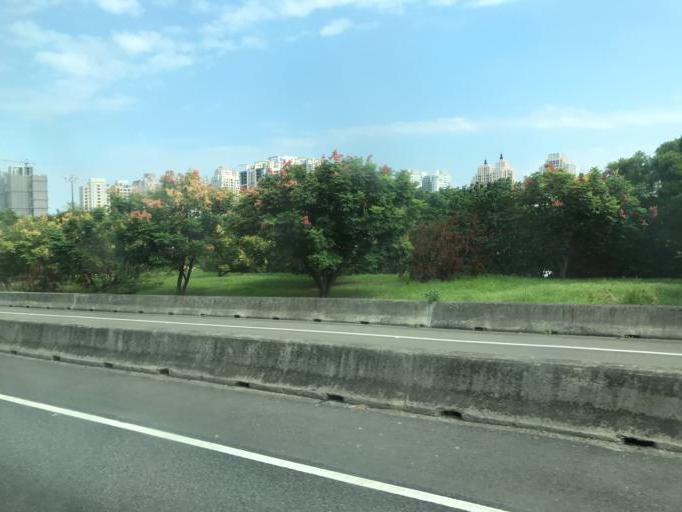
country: TW
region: Taiwan
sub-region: Hsinchu
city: Hsinchu
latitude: 24.7884
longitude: 121.0049
